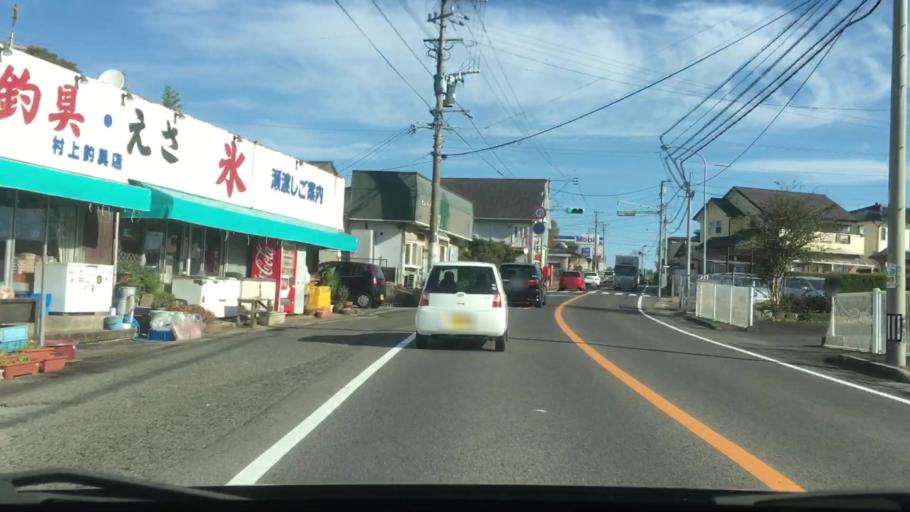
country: JP
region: Nagasaki
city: Sasebo
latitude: 33.0569
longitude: 129.7618
